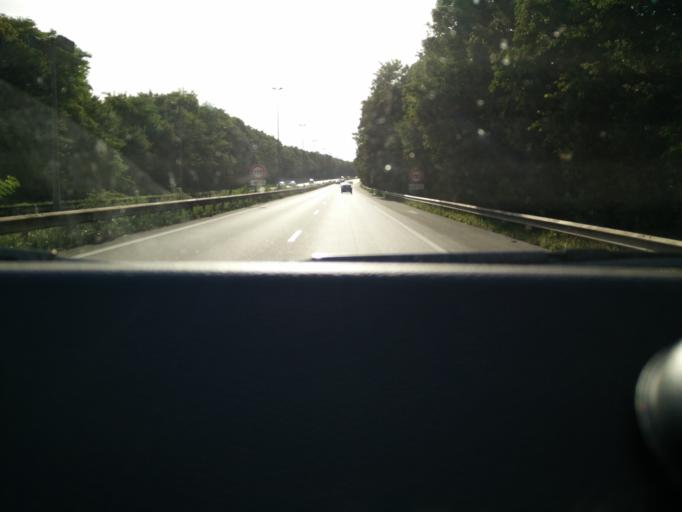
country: FR
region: Nord-Pas-de-Calais
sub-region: Departement du Pas-de-Calais
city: Courcelles-les-Lens
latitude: 50.4244
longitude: 3.0157
